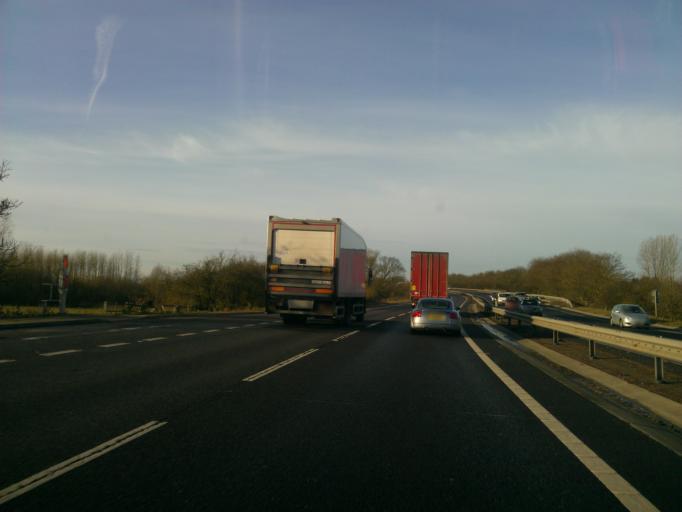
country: GB
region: England
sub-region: Essex
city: Kelvedon
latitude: 51.8269
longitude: 0.6961
